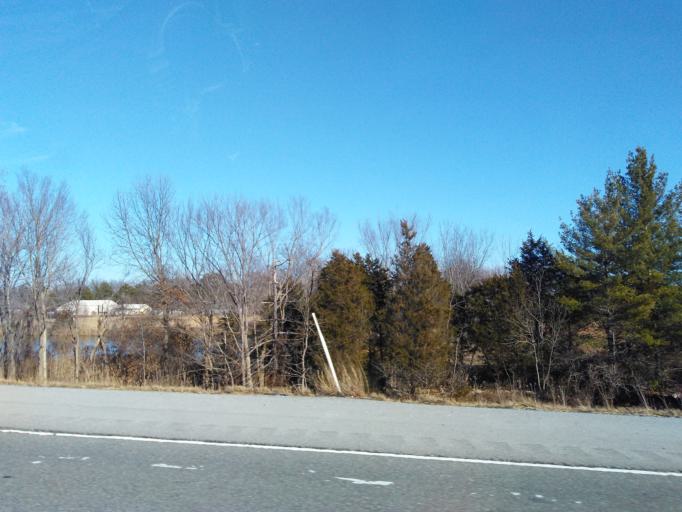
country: US
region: Illinois
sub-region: Williamson County
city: Johnston City
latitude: 37.8018
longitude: -88.9457
